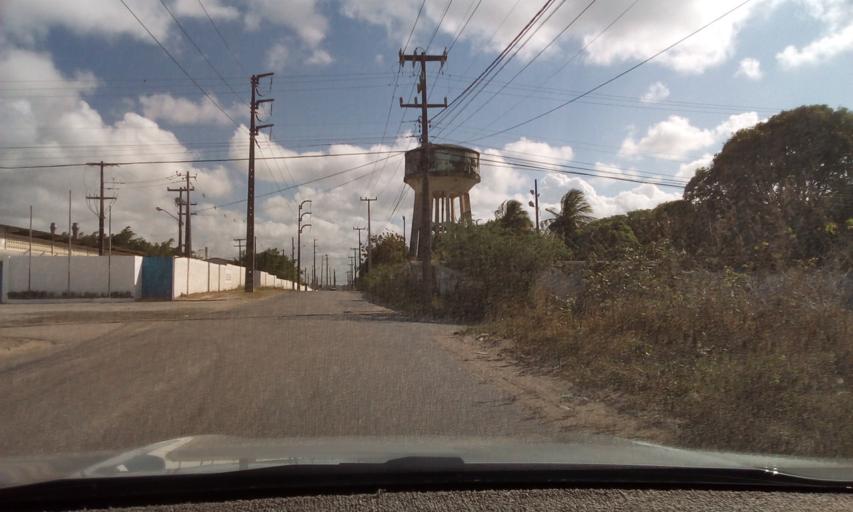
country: BR
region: Paraiba
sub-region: Bayeux
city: Bayeux
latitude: -7.1752
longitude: -34.9076
